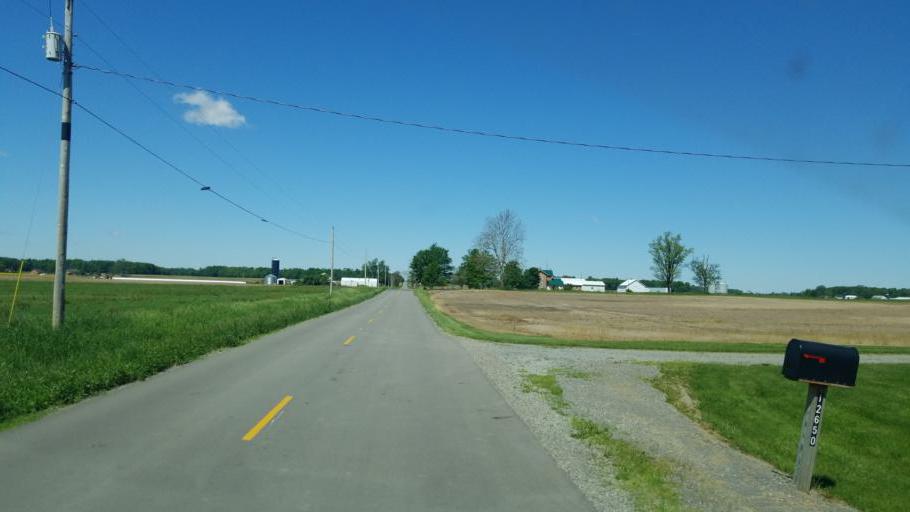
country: US
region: Ohio
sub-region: Shelby County
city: Jackson Center
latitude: 40.4174
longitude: -83.9814
